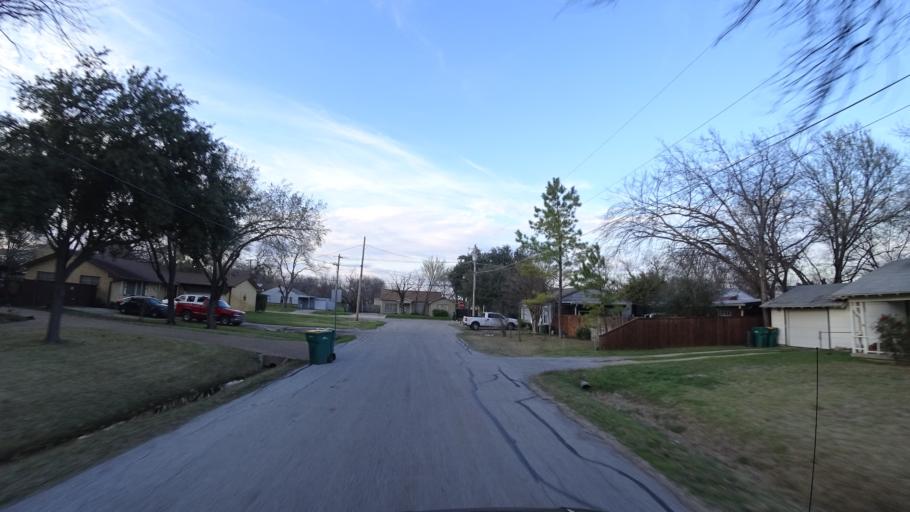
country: US
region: Texas
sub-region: Denton County
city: Lewisville
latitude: 33.0488
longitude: -97.0028
